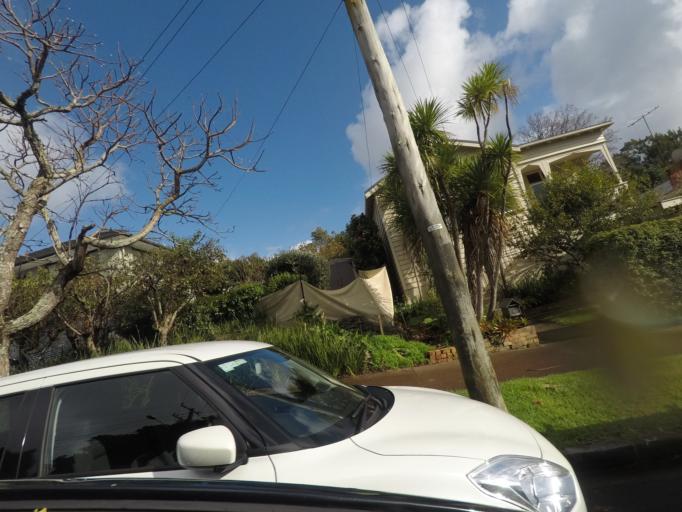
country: NZ
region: Auckland
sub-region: Auckland
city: Auckland
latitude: -36.8588
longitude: 174.7365
